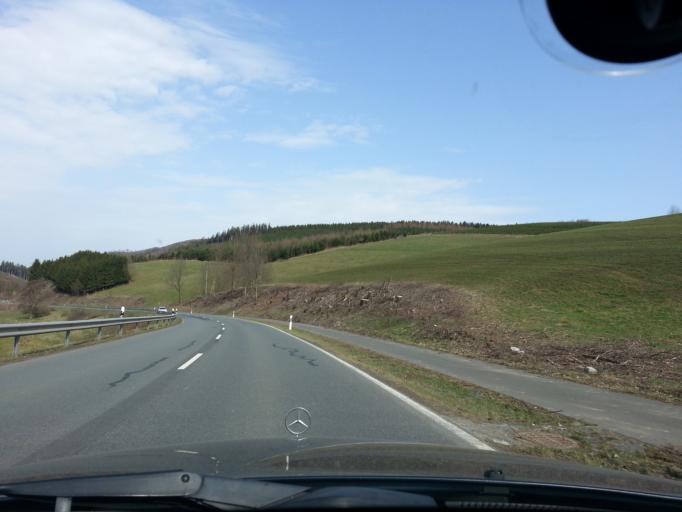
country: DE
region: North Rhine-Westphalia
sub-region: Regierungsbezirk Arnsberg
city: Bad Fredeburg
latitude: 51.2628
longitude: 8.3623
